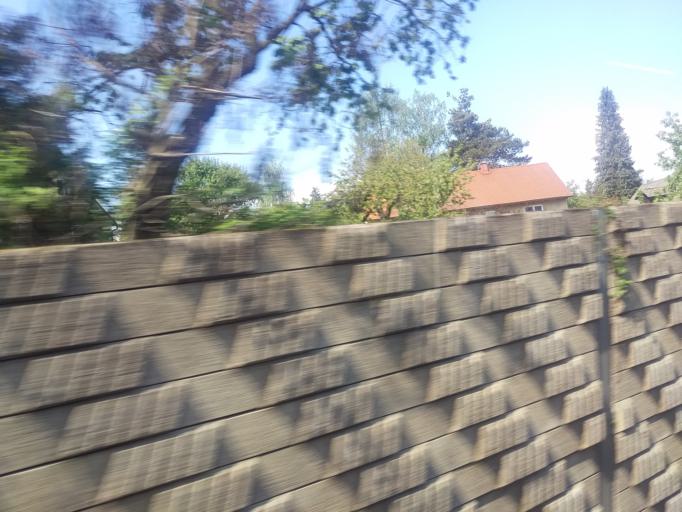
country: AT
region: Styria
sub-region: Politischer Bezirk Graz-Umgebung
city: Gratkorn
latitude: 47.1203
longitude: 15.3392
